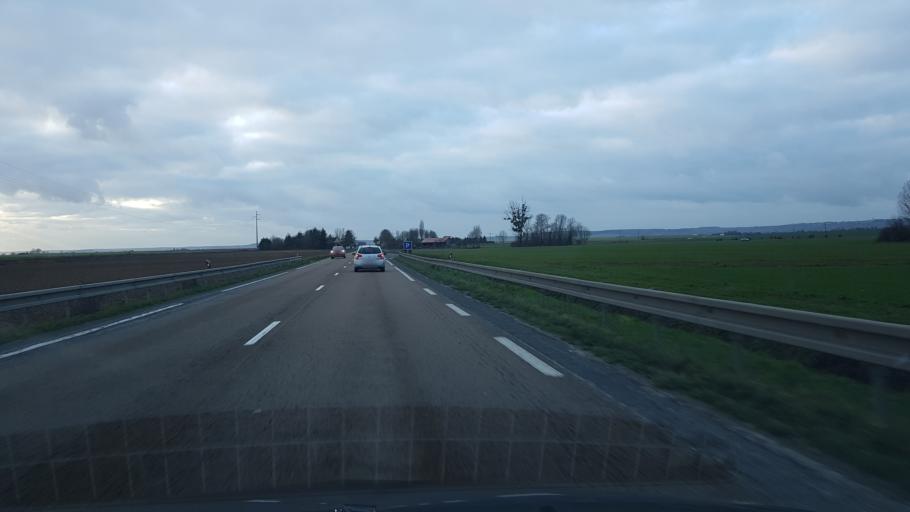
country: FR
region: Champagne-Ardenne
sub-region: Departement de la Marne
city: Connantre
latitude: 48.7265
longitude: 3.8476
